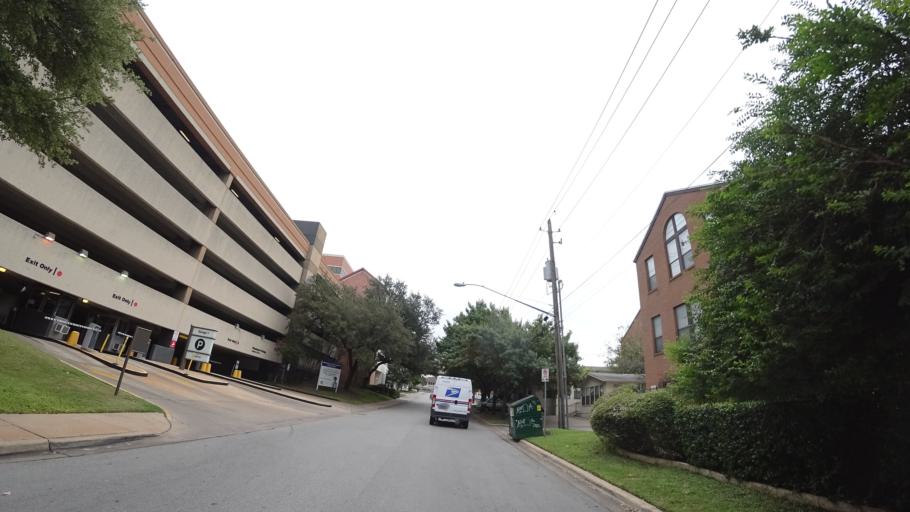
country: US
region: Texas
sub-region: Travis County
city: Austin
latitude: 30.2885
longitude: -97.7255
